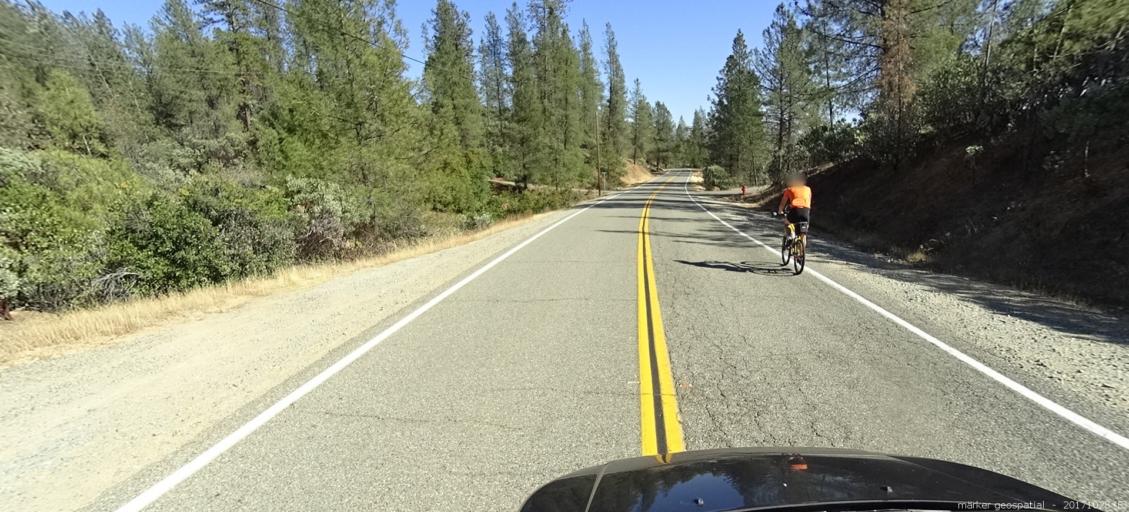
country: US
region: California
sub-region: Shasta County
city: Shasta
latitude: 40.6179
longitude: -122.4809
